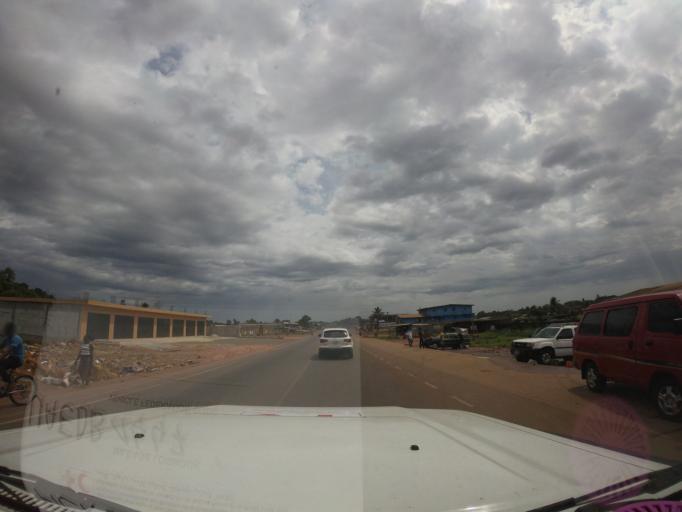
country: LR
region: Montserrado
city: Monrovia
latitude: 6.3027
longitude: -10.6762
